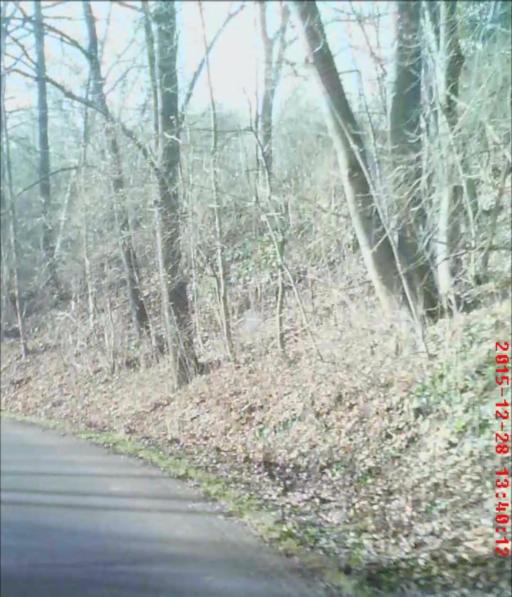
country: DE
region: Thuringia
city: Eberstedt
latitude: 51.0770
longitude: 11.5912
